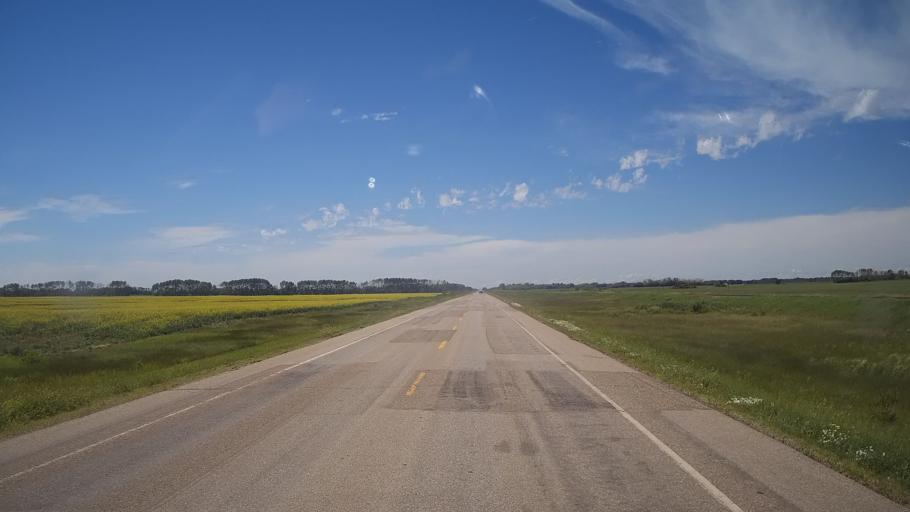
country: CA
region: Saskatchewan
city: Langenburg
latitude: 50.7867
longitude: -101.5365
